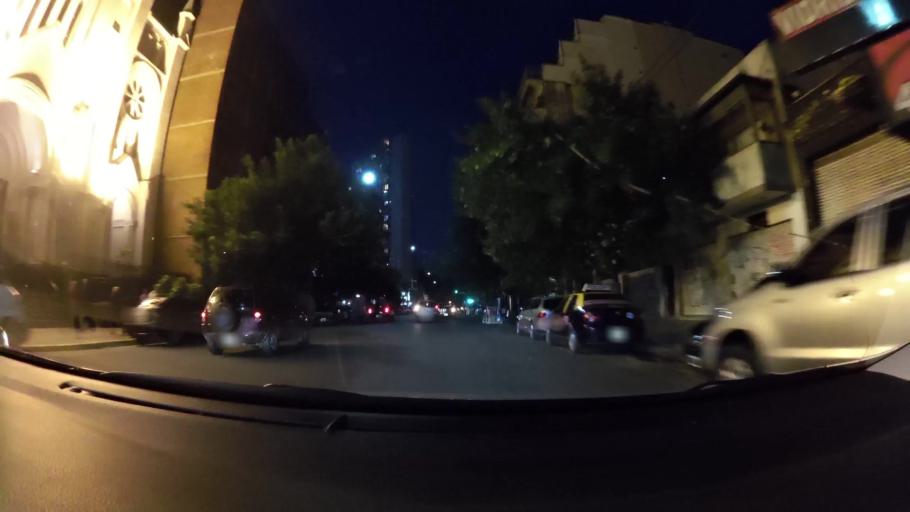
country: AR
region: Buenos Aires F.D.
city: Villa Santa Rita
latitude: -34.6038
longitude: -58.4644
